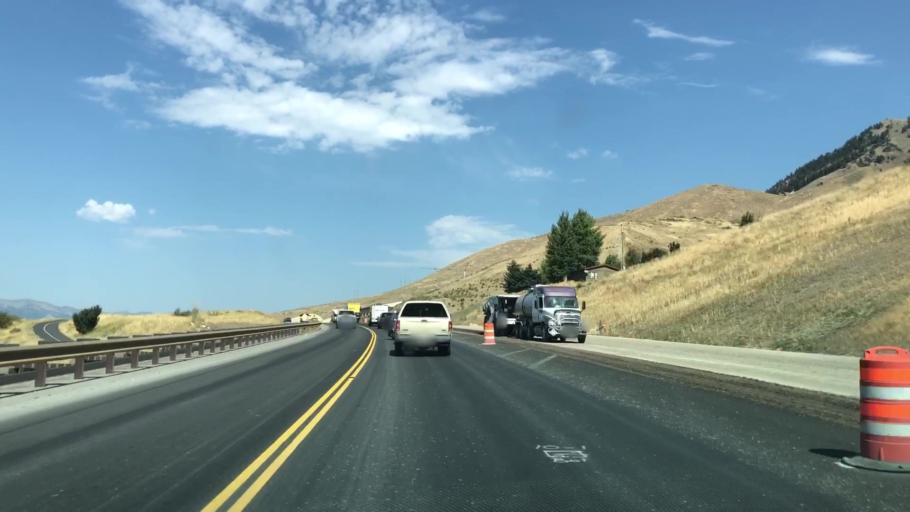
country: US
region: Wyoming
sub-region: Teton County
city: South Park
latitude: 43.3979
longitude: -110.7502
